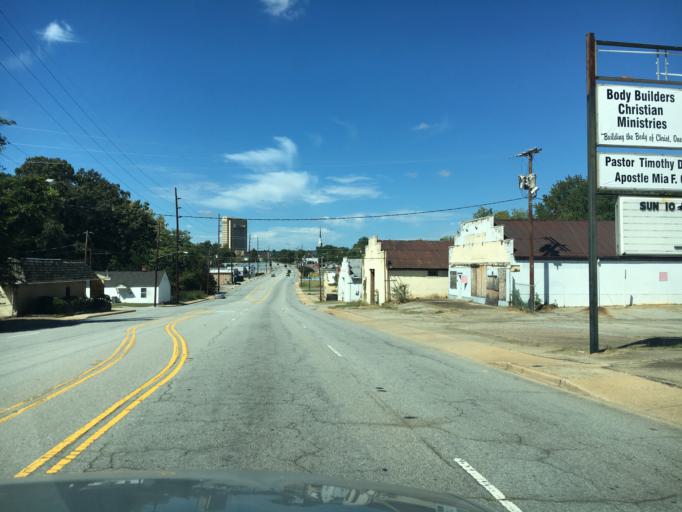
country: US
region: South Carolina
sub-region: Spartanburg County
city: Spartanburg
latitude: 34.9449
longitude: -81.9183
